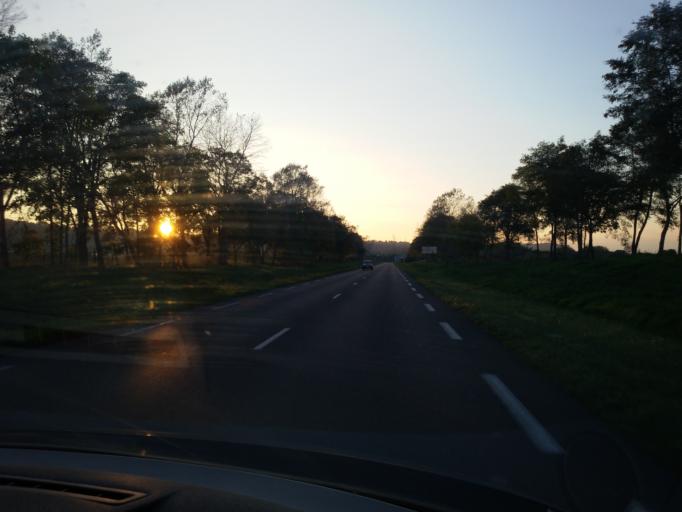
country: FR
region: Lower Normandy
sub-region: Departement du Calvados
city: La Riviere-Saint-Sauveur
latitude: 49.4125
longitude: 0.2808
